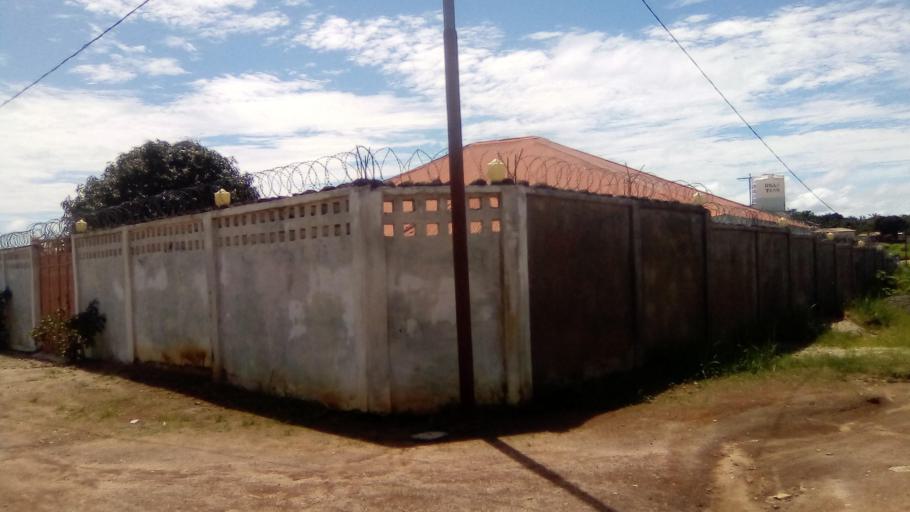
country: SL
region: Eastern Province
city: Simbakoro
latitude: 8.6360
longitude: -10.9982
